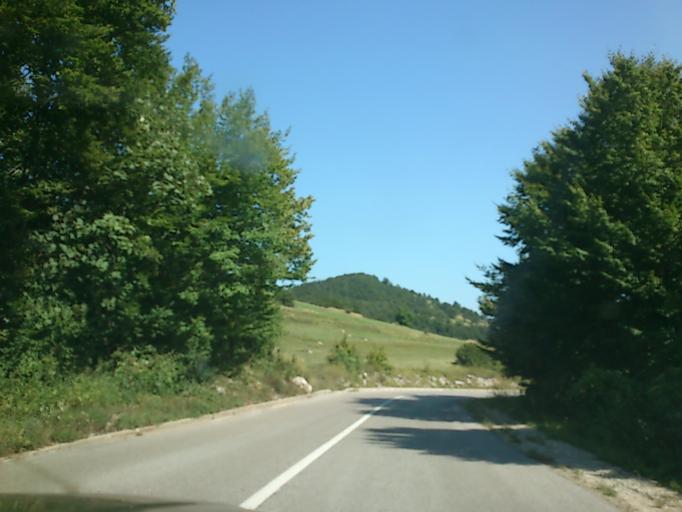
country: HR
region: Licko-Senjska
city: Otocac
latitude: 44.8460
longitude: 15.1162
